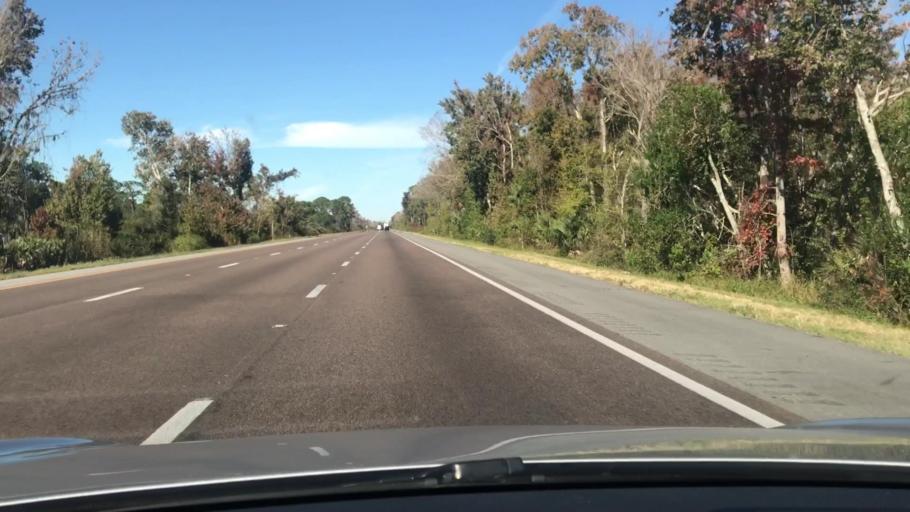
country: US
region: Florida
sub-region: Volusia County
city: Oak Hill
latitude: 28.8866
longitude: -80.9254
